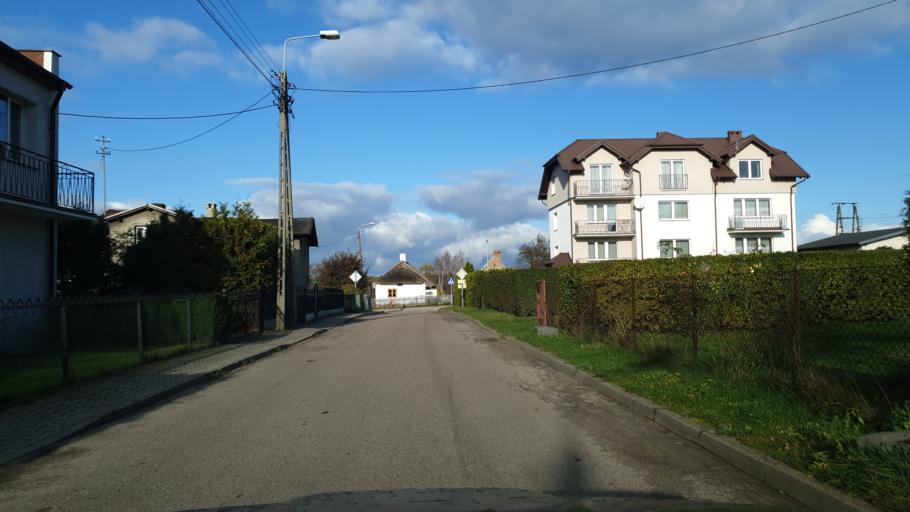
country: PL
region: Pomeranian Voivodeship
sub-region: Powiat pucki
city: Jastrzebia Gora
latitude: 54.8246
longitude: 18.2487
